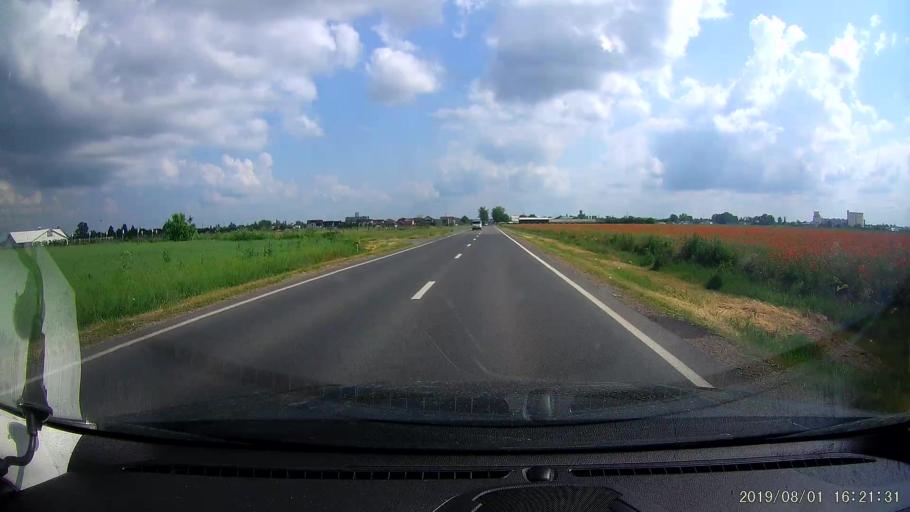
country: RO
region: Calarasi
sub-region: Municipiul Calarasi
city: Calarasi
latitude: 44.2164
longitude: 27.3400
